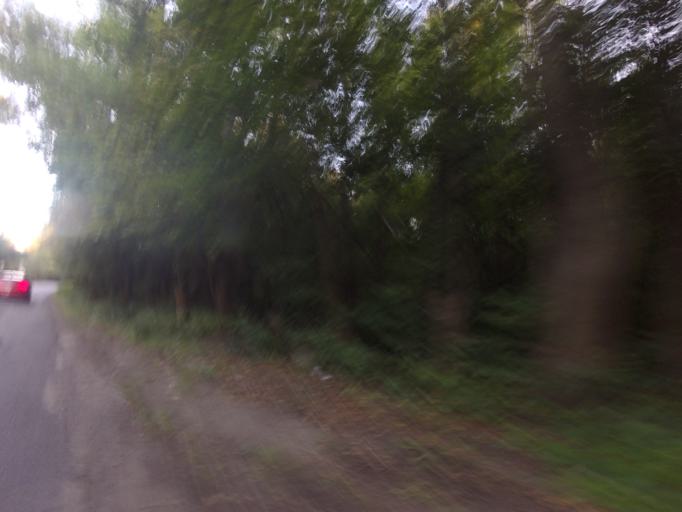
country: CA
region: Quebec
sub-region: Laurentides
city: Oka
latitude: 45.4519
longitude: -74.1139
